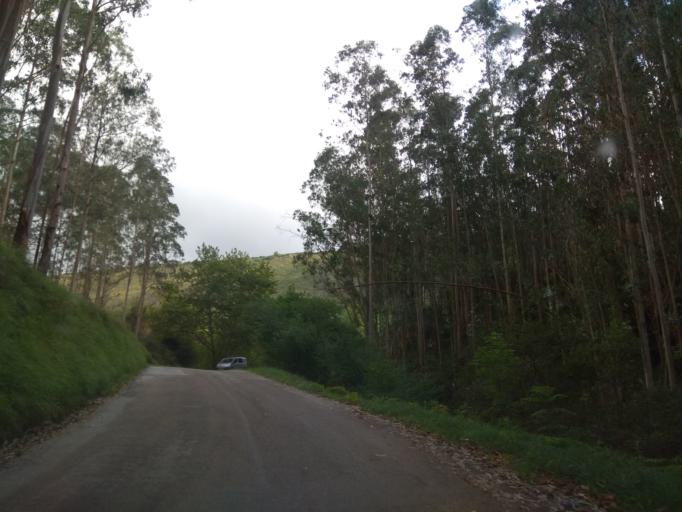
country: ES
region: Cantabria
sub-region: Provincia de Cantabria
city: San Vicente de la Barquera
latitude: 43.3155
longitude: -4.3922
